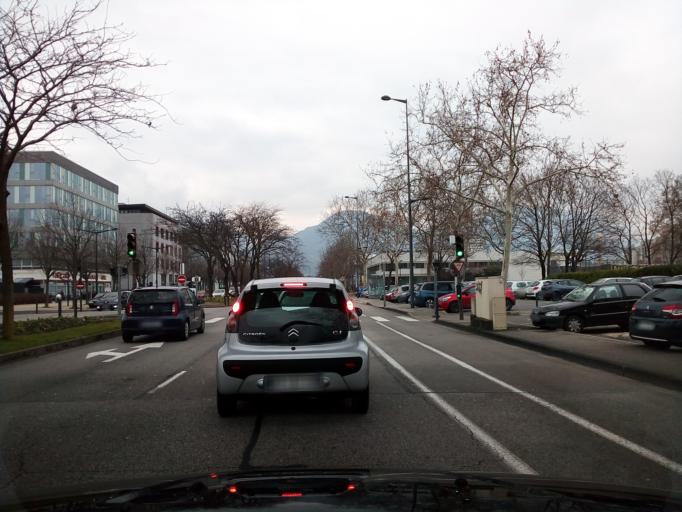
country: FR
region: Rhone-Alpes
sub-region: Departement de l'Isere
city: Grenoble
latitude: 45.1636
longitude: 5.7289
